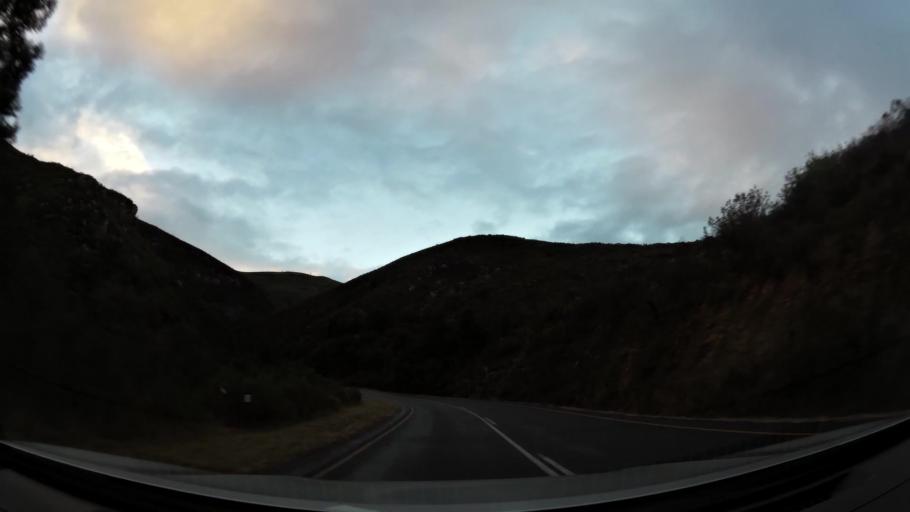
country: ZA
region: Western Cape
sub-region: Overberg District Municipality
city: Swellendam
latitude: -33.9860
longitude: 20.7194
